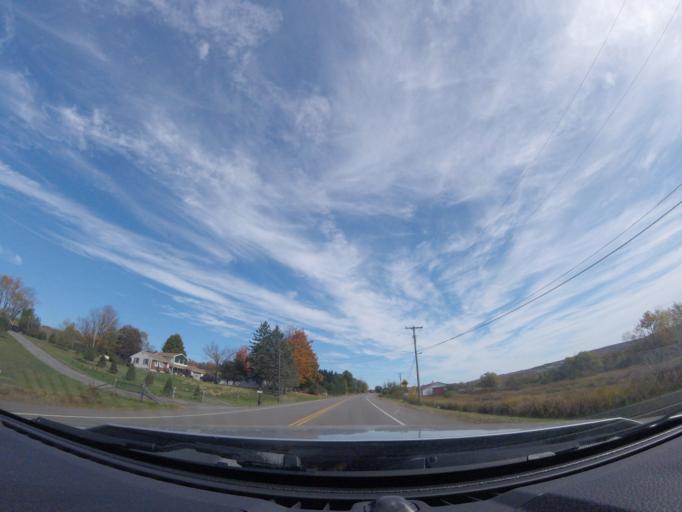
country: US
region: New York
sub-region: Cortland County
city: Cortland West
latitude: 42.5566
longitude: -76.2809
